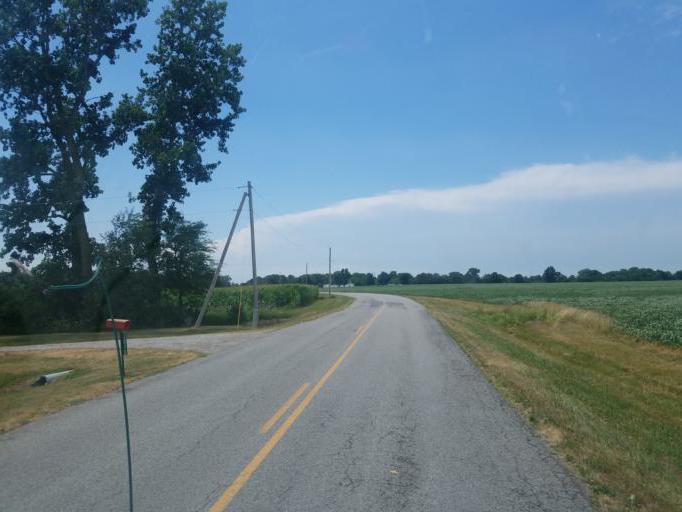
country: US
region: Ohio
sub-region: Paulding County
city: Antwerp
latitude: 41.1991
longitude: -84.7508
